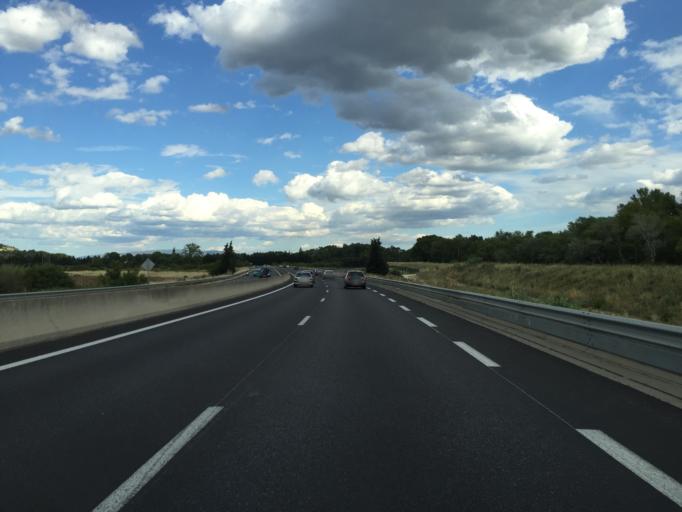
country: FR
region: Provence-Alpes-Cote d'Azur
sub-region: Departement des Bouches-du-Rhone
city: Noves
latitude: 43.8947
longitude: 4.9005
